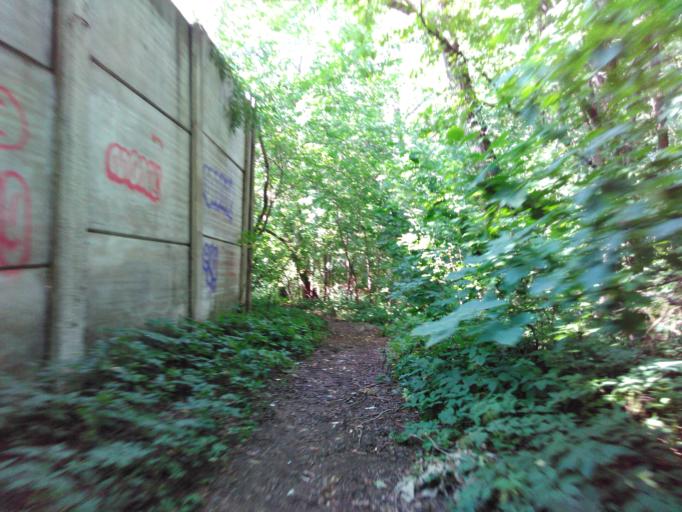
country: RU
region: Moskovskaya
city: Bol'shaya Setun'
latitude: 55.7108
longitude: 37.4157
